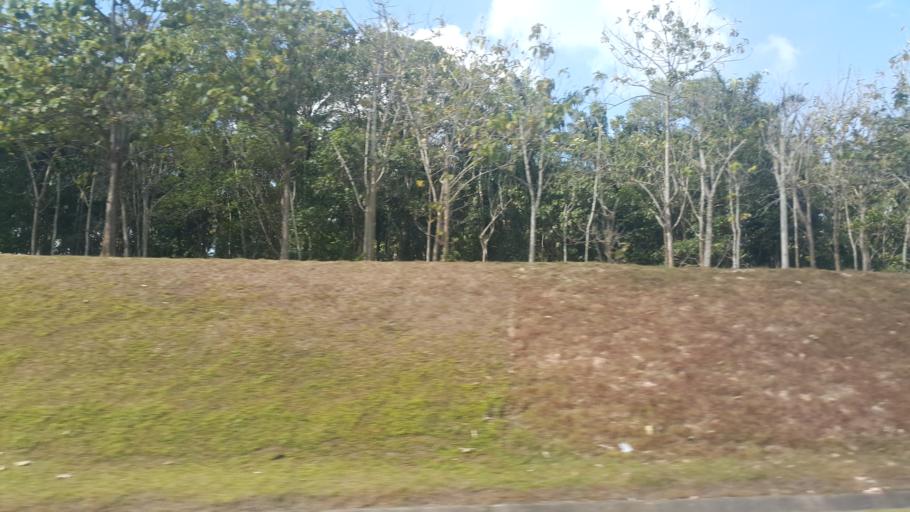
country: MY
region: Johor
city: Parit Raja
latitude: 1.9135
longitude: 103.2064
